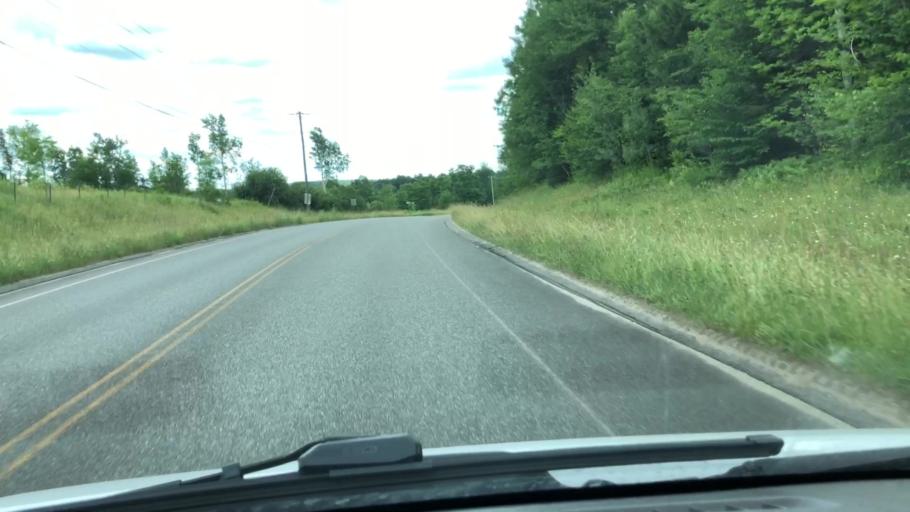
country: US
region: Massachusetts
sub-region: Berkshire County
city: Adams
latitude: 42.5376
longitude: -73.0555
